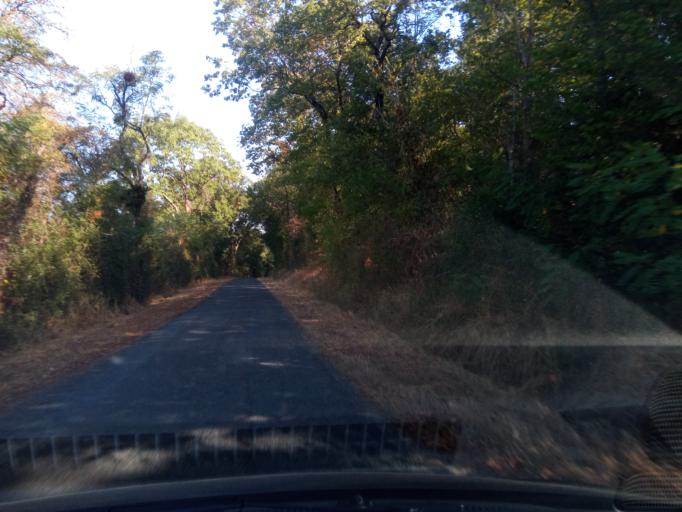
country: FR
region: Poitou-Charentes
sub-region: Departement de la Vienne
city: Saulge
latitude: 46.3739
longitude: 0.8715
